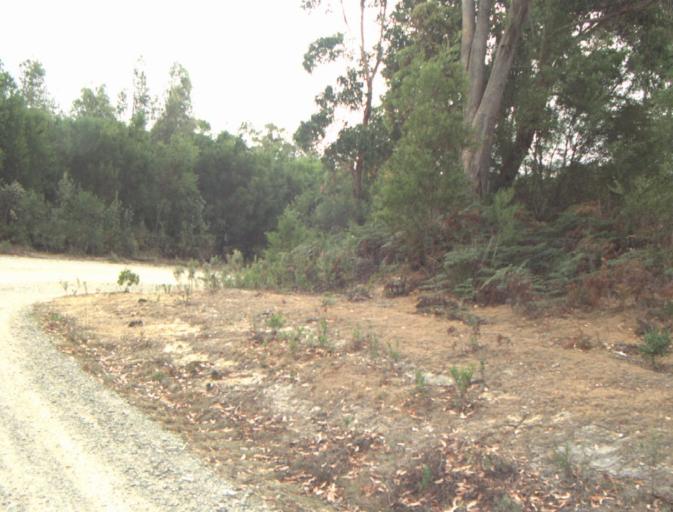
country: AU
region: Tasmania
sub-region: Launceston
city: Mayfield
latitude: -41.1585
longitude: 147.1712
